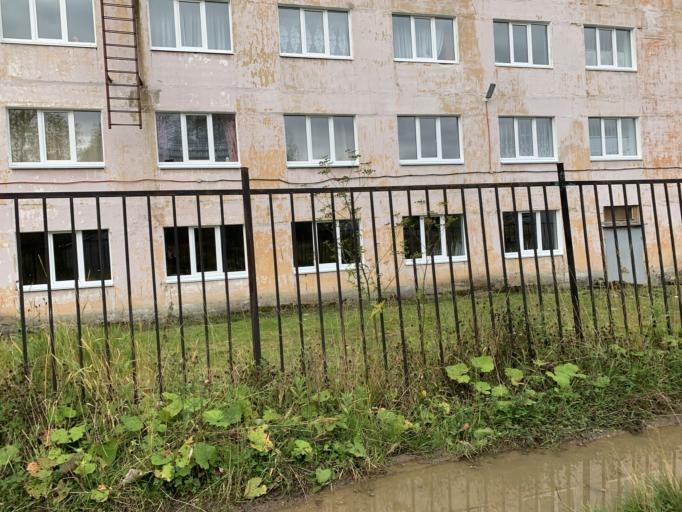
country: RU
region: Perm
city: Gubakha
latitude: 58.8315
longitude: 57.5603
